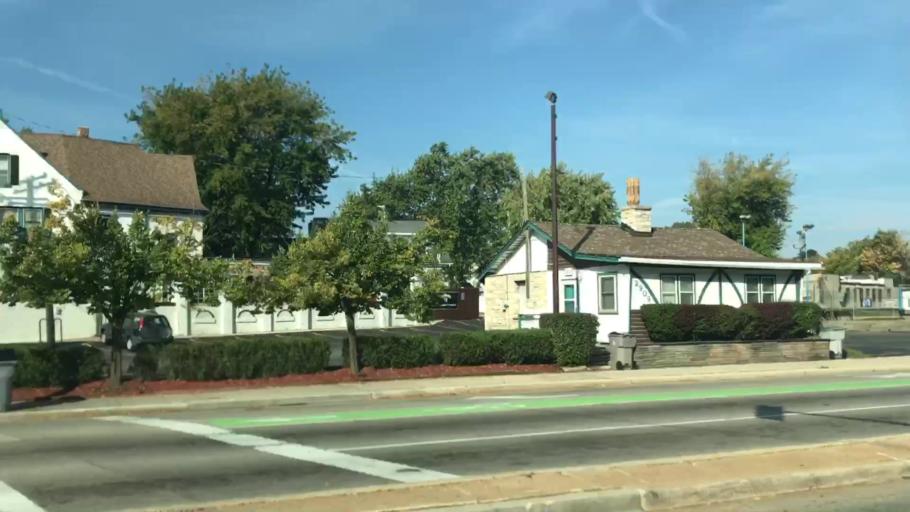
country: US
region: Wisconsin
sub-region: Milwaukee County
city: Shorewood
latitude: 43.0712
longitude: -87.8977
